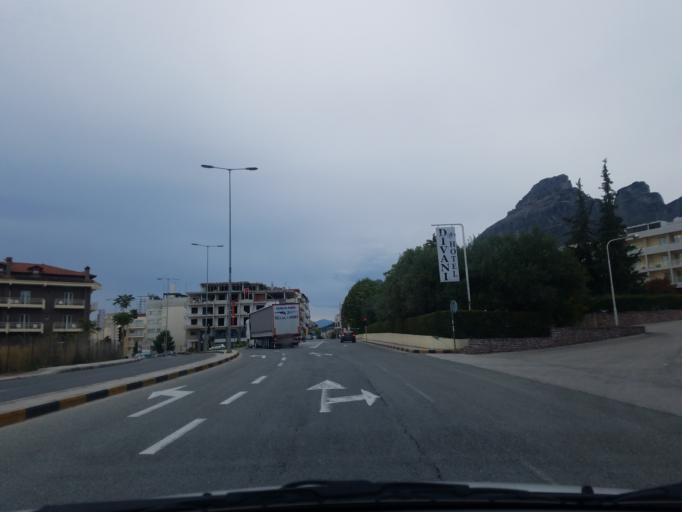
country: GR
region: Thessaly
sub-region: Trikala
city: Kalampaka
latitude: 39.7018
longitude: 21.6336
